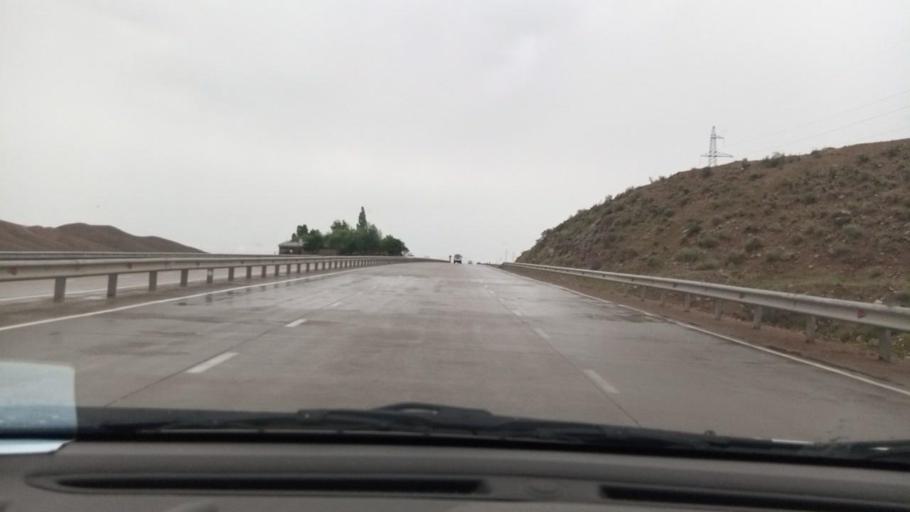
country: UZ
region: Namangan
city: Pop Shahri
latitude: 40.9425
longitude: 70.6878
